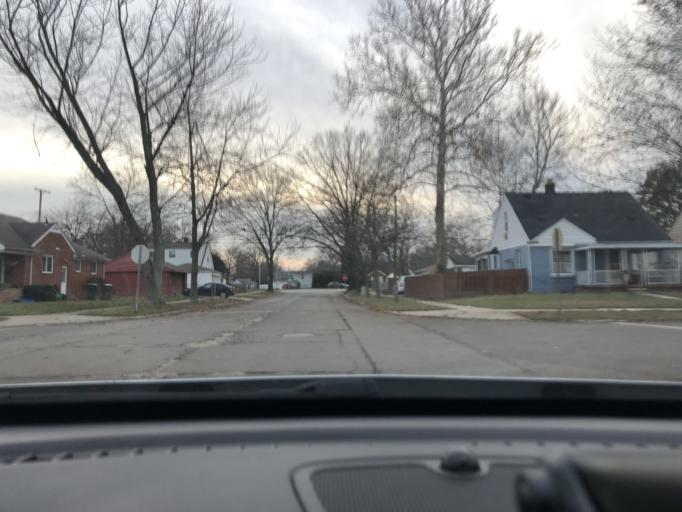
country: US
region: Michigan
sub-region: Wayne County
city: Allen Park
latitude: 42.2818
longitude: -83.2233
